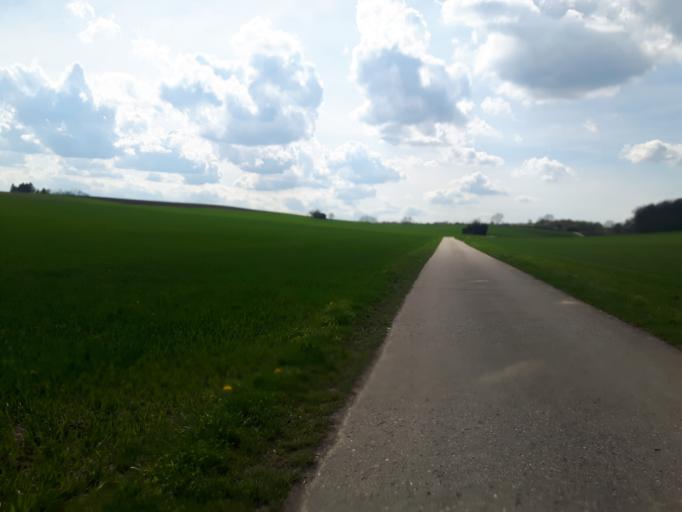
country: DE
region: Baden-Wuerttemberg
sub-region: Regierungsbezirk Stuttgart
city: Gemmingen
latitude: 49.1402
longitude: 9.0150
